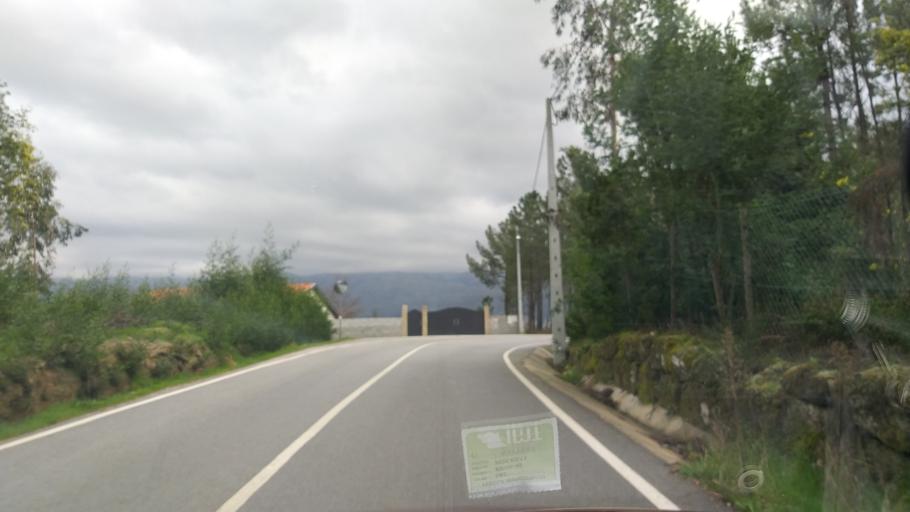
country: PT
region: Guarda
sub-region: Seia
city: Seia
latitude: 40.4785
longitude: -7.6646
